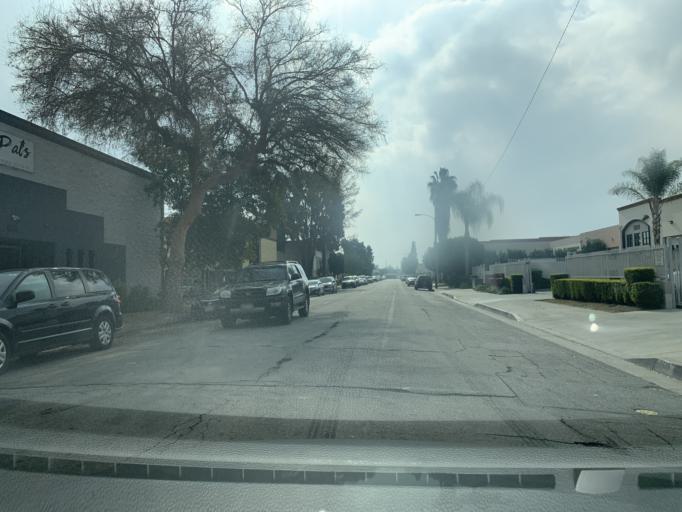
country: US
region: California
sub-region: Los Angeles County
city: South El Monte
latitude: 34.0584
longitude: -118.0500
